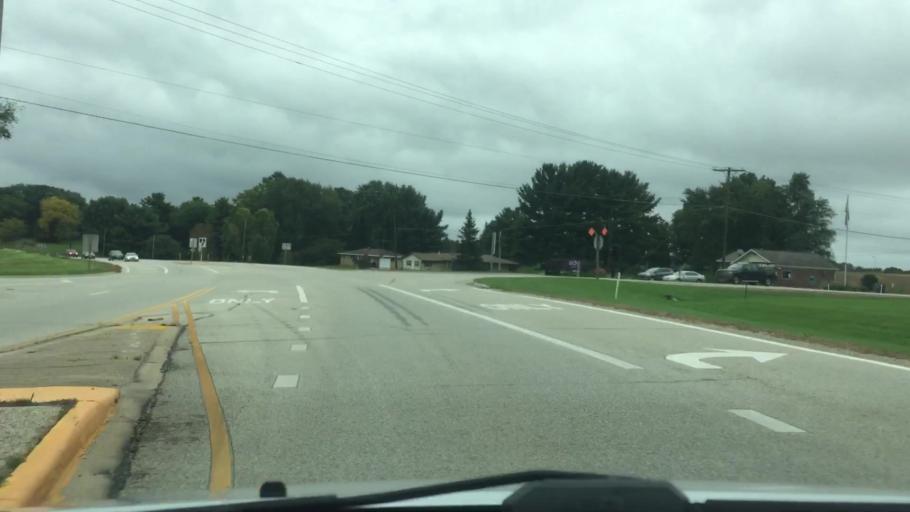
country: US
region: Wisconsin
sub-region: Walworth County
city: Elkhorn
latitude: 42.7420
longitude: -88.5531
